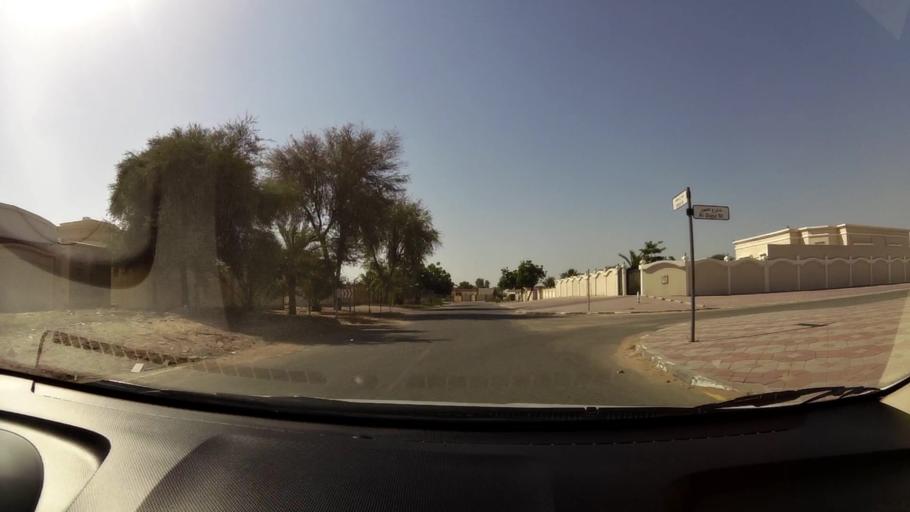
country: AE
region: Umm al Qaywayn
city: Umm al Qaywayn
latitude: 25.4920
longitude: 55.5791
